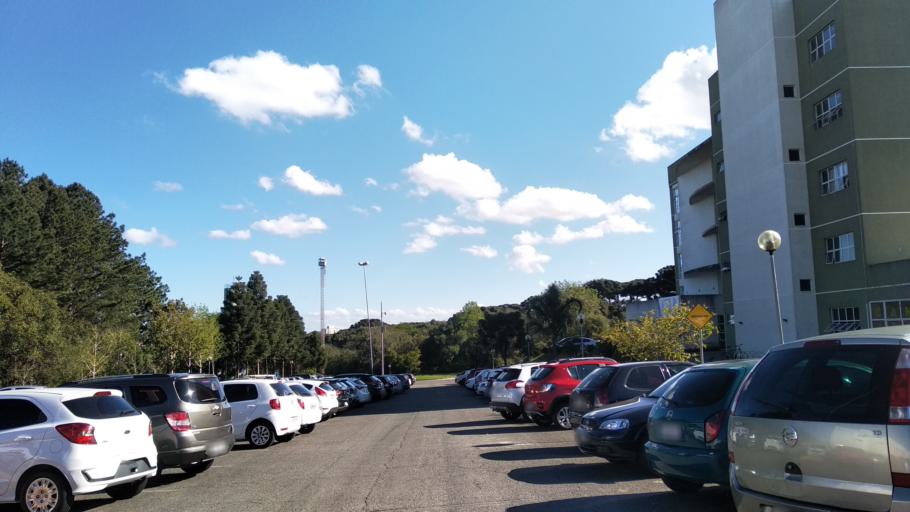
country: BR
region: Parana
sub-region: Curitiba
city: Curitiba
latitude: -25.4445
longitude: -49.2377
